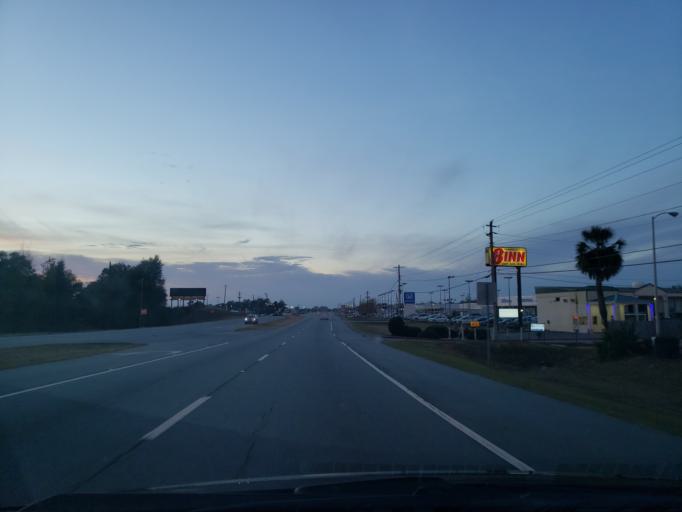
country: US
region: Georgia
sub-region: Dougherty County
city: Albany
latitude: 31.5728
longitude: -84.1290
